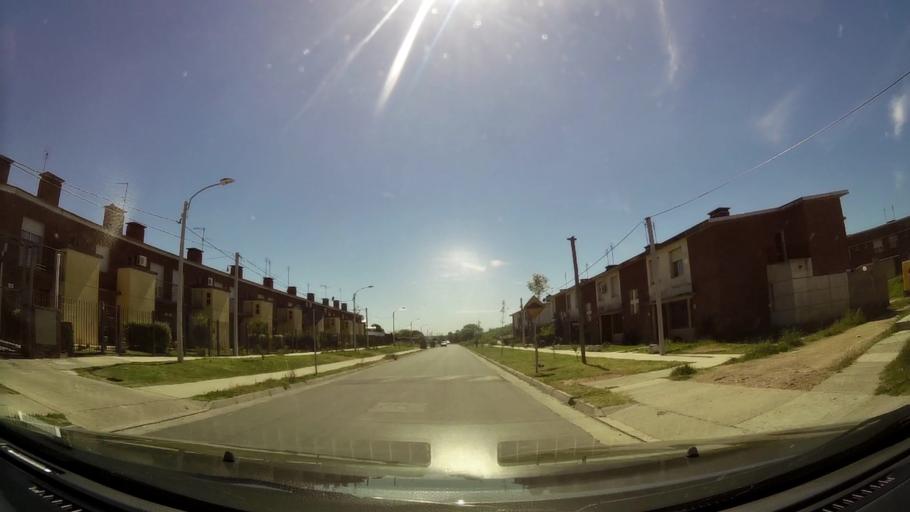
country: UY
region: Canelones
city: Paso de Carrasco
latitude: -34.8609
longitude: -56.1221
